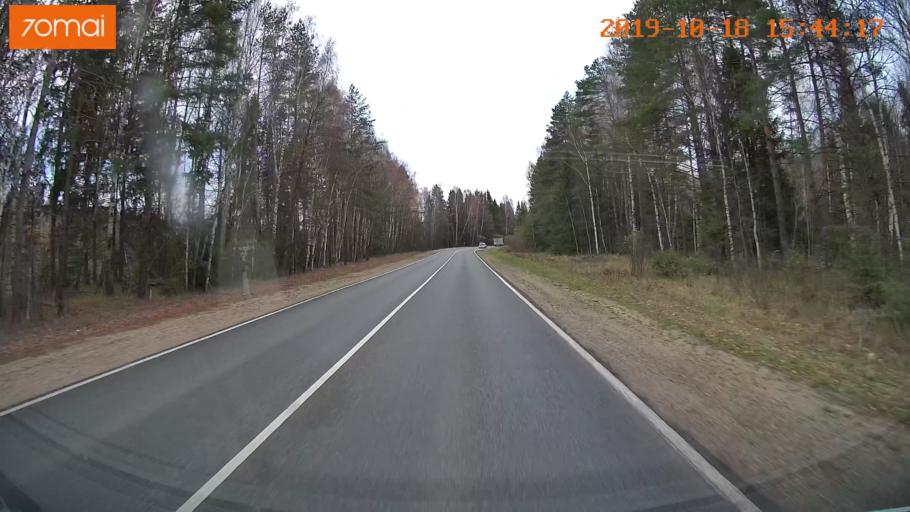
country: RU
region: Vladimir
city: Golovino
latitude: 55.9795
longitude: 40.5480
